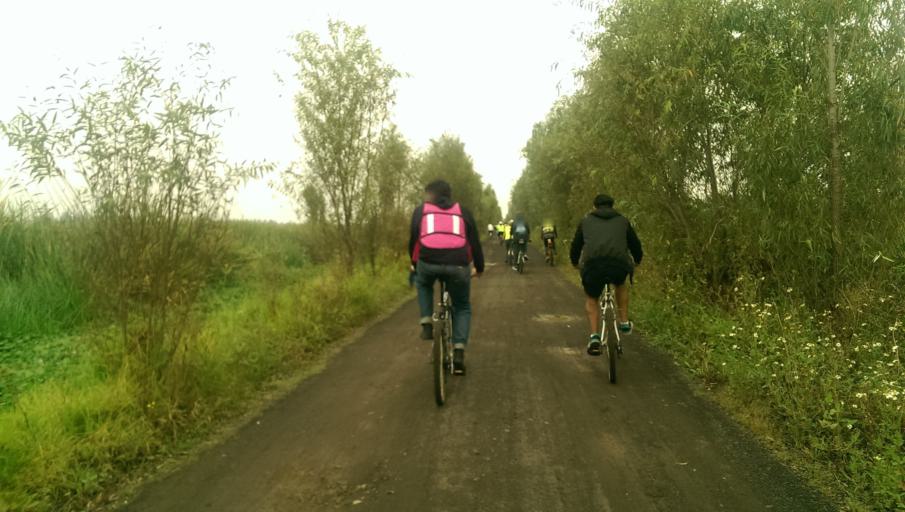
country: MX
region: Mexico City
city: Tlahuac
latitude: 19.2654
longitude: -99.0517
